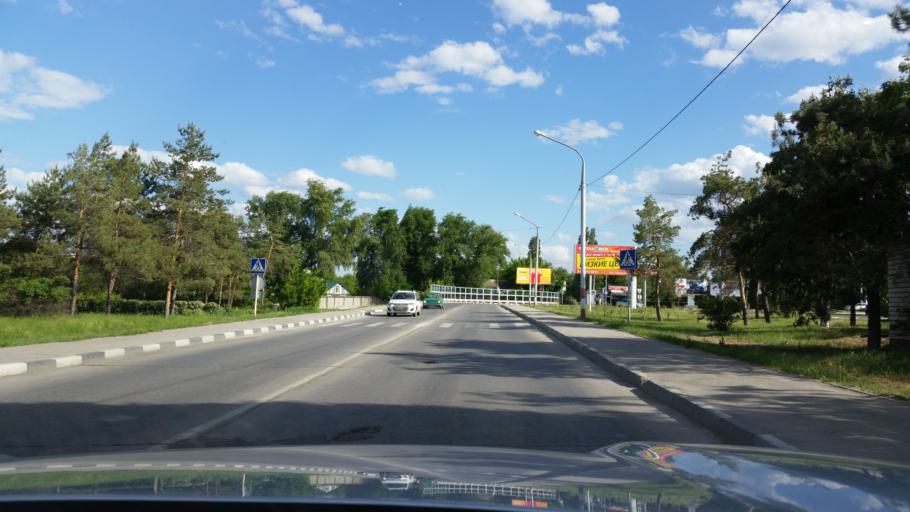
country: RU
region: Saratov
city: Engel's
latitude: 51.5040
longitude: 46.0799
